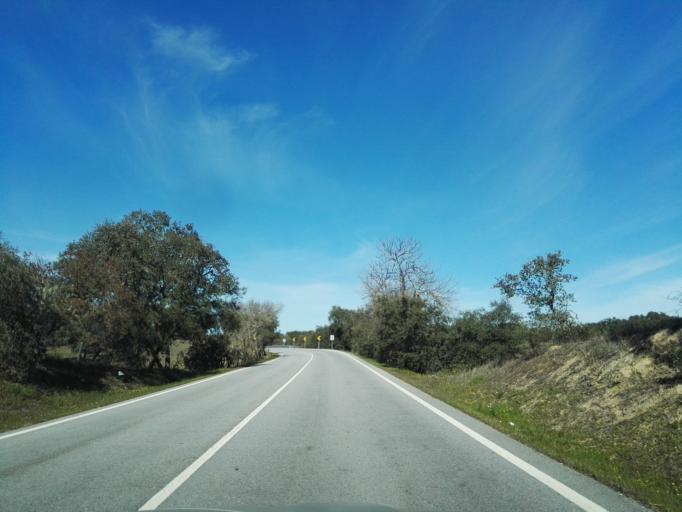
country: PT
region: Portalegre
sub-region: Arronches
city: Arronches
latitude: 39.0740
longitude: -7.2773
